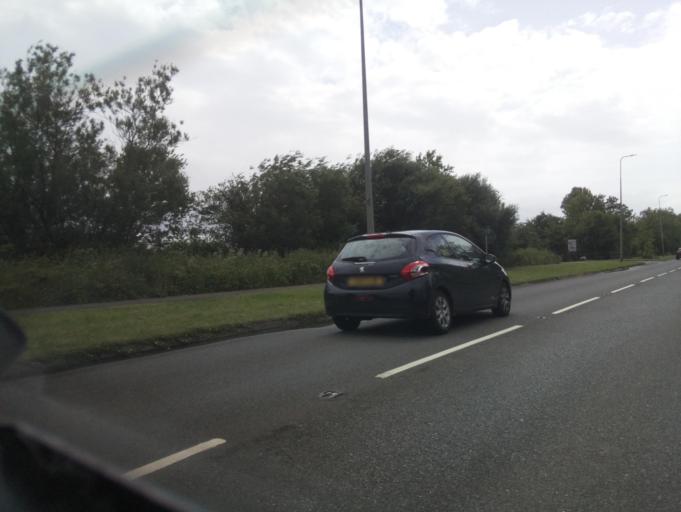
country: GB
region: Wales
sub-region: Vale of Glamorgan
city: Dinas Powys
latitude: 51.4116
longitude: -3.2292
